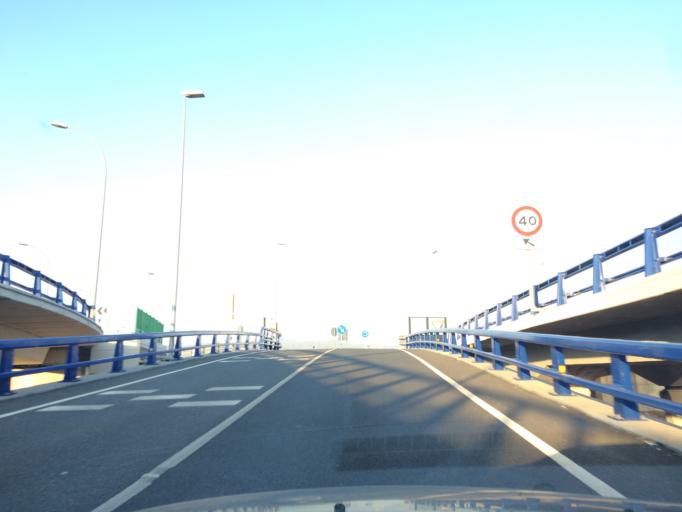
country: ES
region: Andalusia
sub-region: Provincia de Malaga
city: Torremolinos
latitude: 36.6745
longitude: -4.4857
